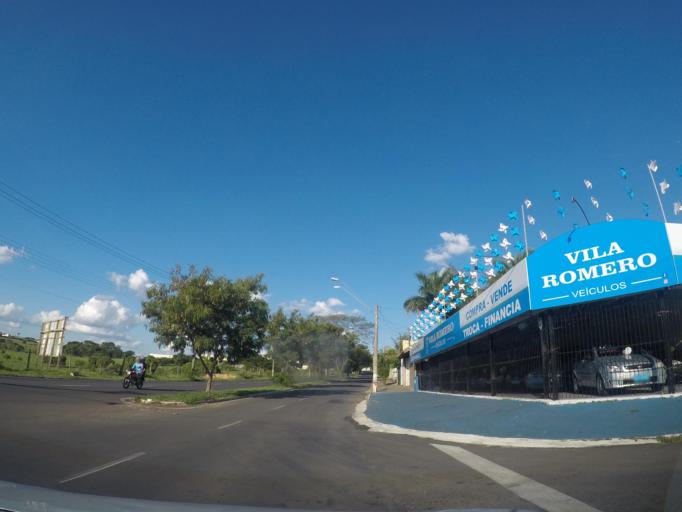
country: BR
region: Sao Paulo
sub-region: Sumare
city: Sumare
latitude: -22.8077
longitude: -47.2269
